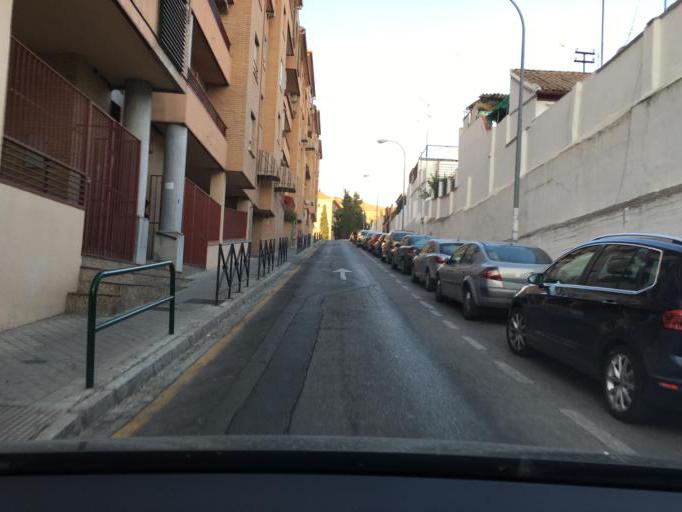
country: ES
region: Andalusia
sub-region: Provincia de Granada
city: Granada
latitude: 37.1903
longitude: -3.6036
